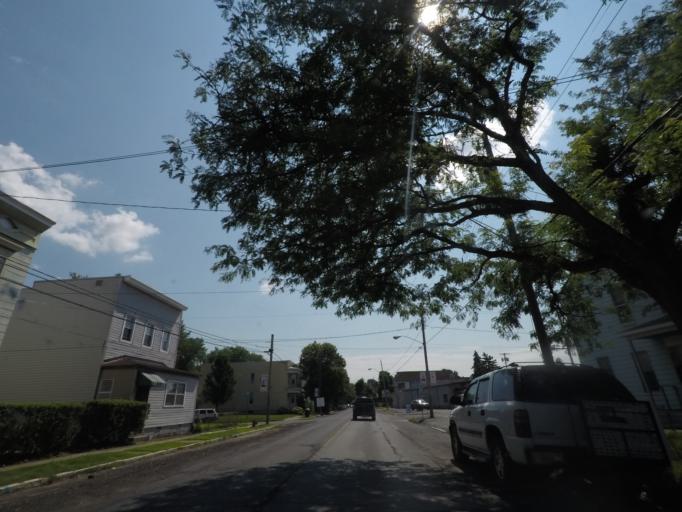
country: US
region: New York
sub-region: Albany County
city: Watervliet
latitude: 42.7105
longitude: -73.7095
